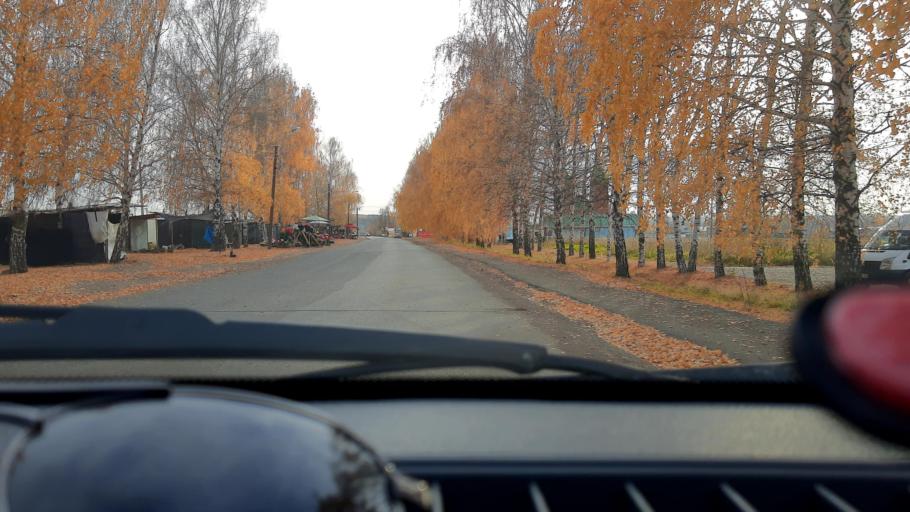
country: RU
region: Bashkortostan
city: Ufa
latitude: 54.8490
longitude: 56.1539
